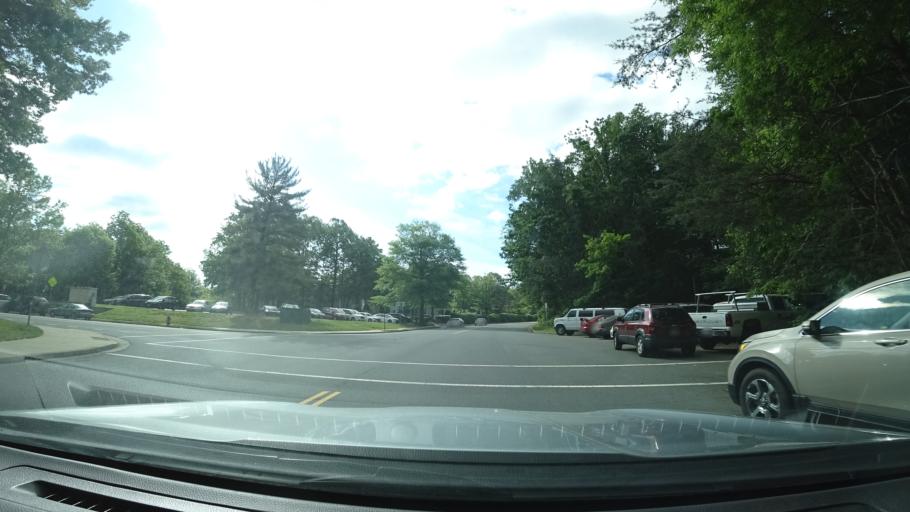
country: US
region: Virginia
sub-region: Fairfax County
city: Herndon
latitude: 38.9412
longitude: -77.3674
